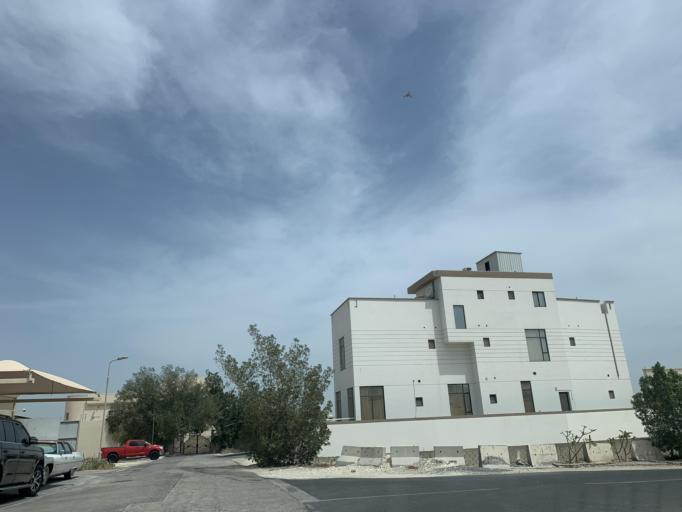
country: BH
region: Northern
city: Ar Rifa'
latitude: 26.1448
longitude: 50.5654
